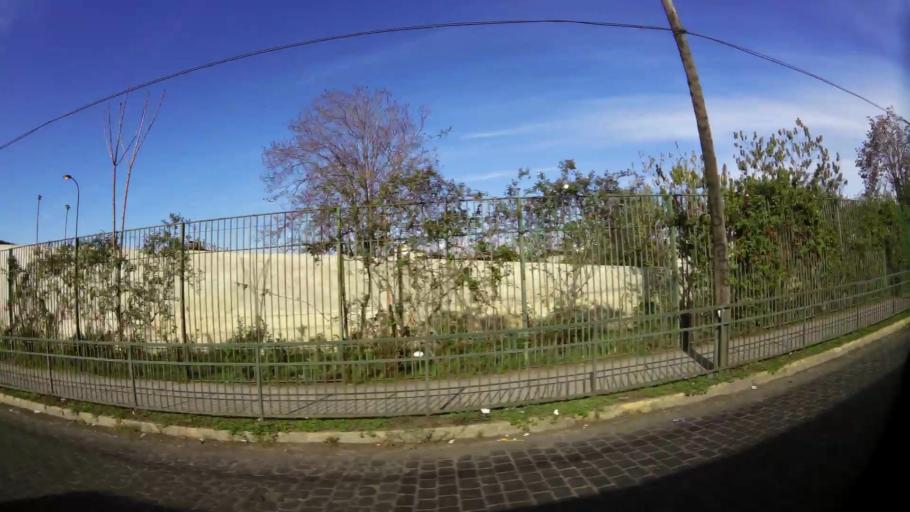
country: CL
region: Santiago Metropolitan
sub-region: Provincia de Santiago
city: Santiago
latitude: -33.4563
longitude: -70.6805
